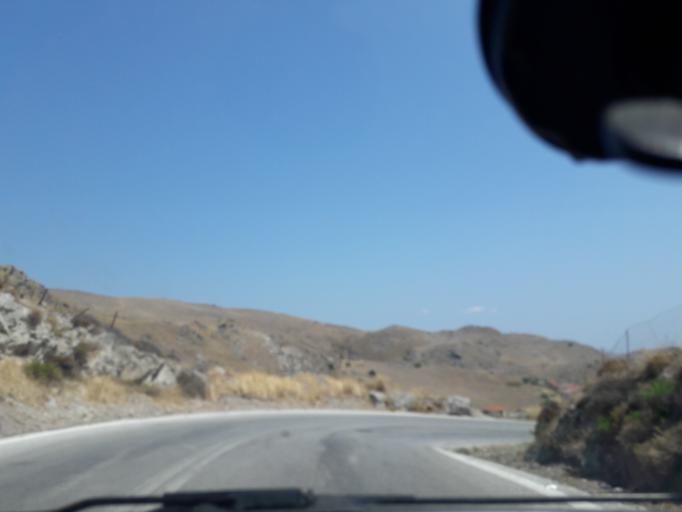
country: GR
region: North Aegean
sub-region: Nomos Lesvou
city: Myrina
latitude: 39.8606
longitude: 25.0792
